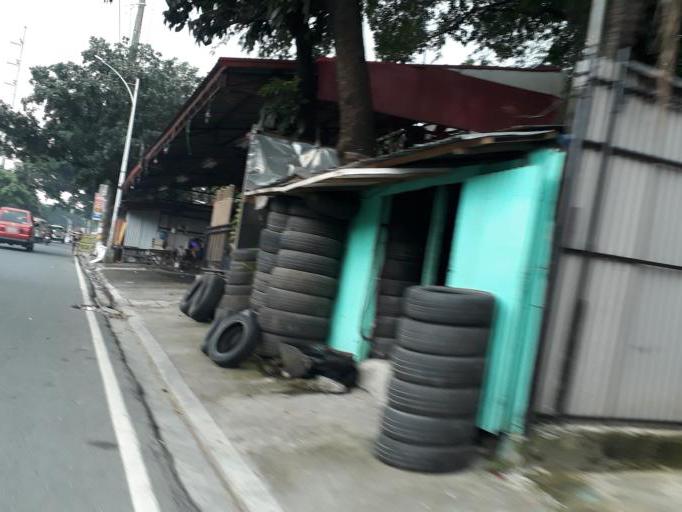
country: PH
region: Calabarzon
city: Bagong Pagasa
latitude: 14.6709
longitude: 121.0519
